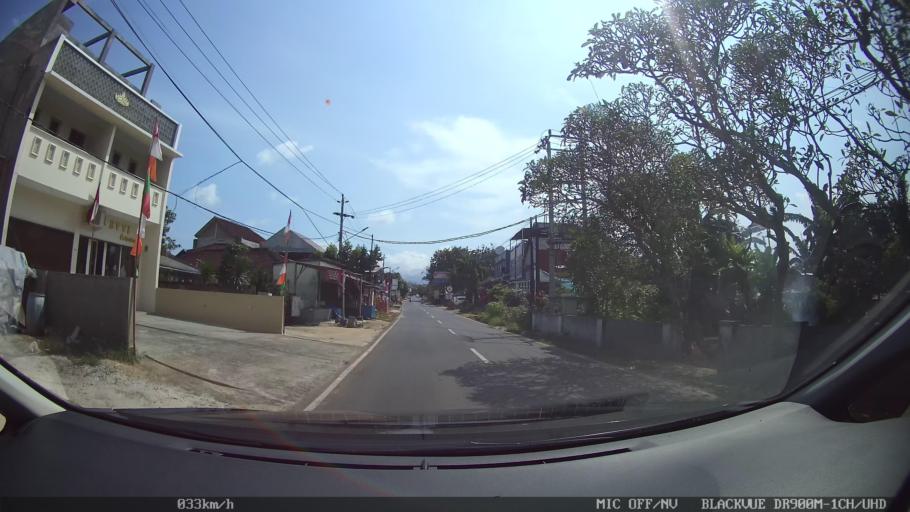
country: ID
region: Lampung
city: Kedaton
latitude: -5.3864
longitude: 105.2432
